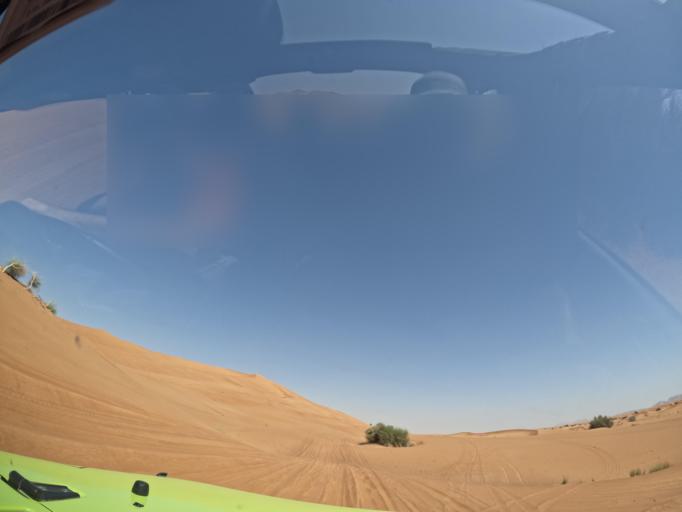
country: AE
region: Ash Shariqah
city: Adh Dhayd
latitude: 24.9696
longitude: 55.7203
